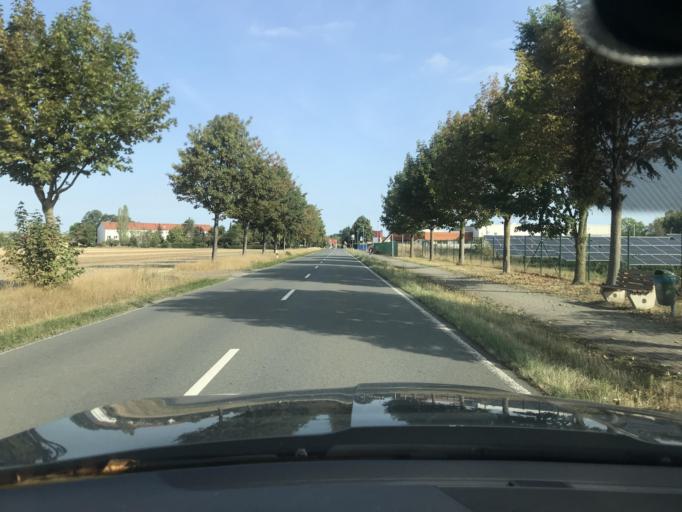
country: DE
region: Saxony-Anhalt
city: Gross Quenstedt
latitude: 51.9246
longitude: 11.1415
